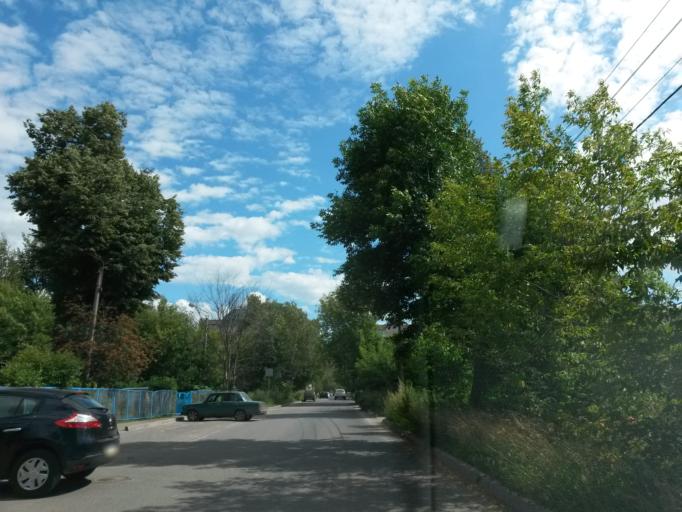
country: RU
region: Ivanovo
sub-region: Gorod Ivanovo
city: Ivanovo
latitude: 56.9932
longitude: 40.9697
